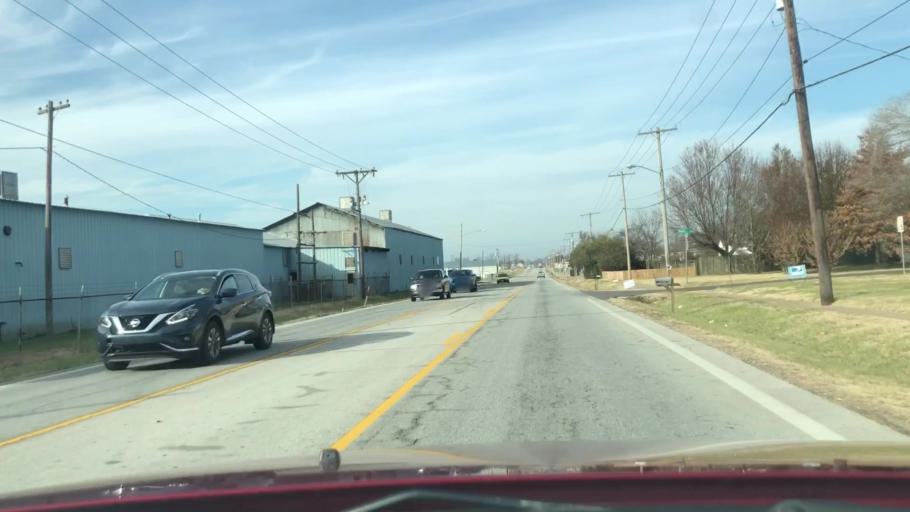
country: US
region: Missouri
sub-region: Greene County
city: Springfield
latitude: 37.2251
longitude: -93.2481
